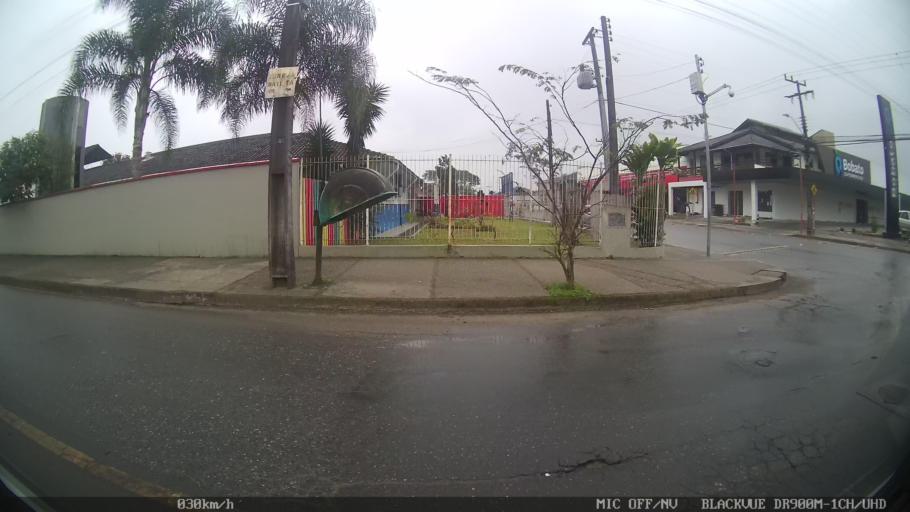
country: BR
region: Santa Catarina
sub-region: Joinville
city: Joinville
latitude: -26.2127
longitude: -48.8237
